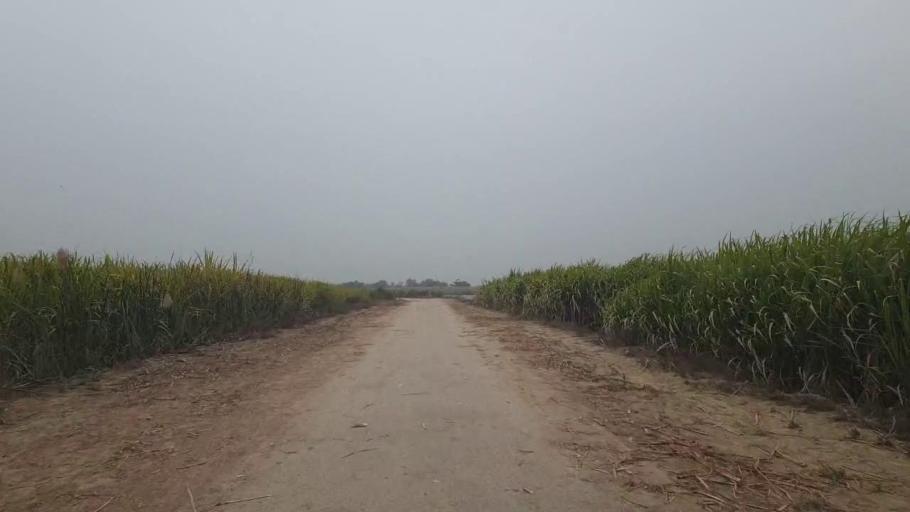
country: PK
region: Sindh
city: Shahdadpur
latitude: 25.8665
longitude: 68.6132
